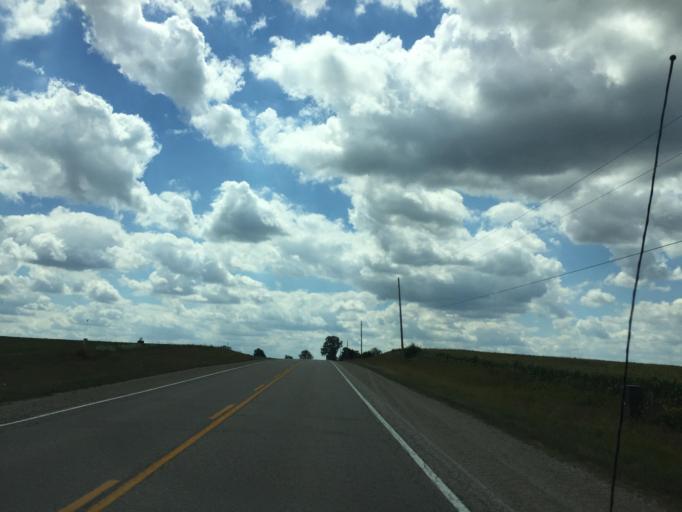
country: CA
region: Ontario
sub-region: Wellington County
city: Guelph
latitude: 43.5394
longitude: -80.3634
